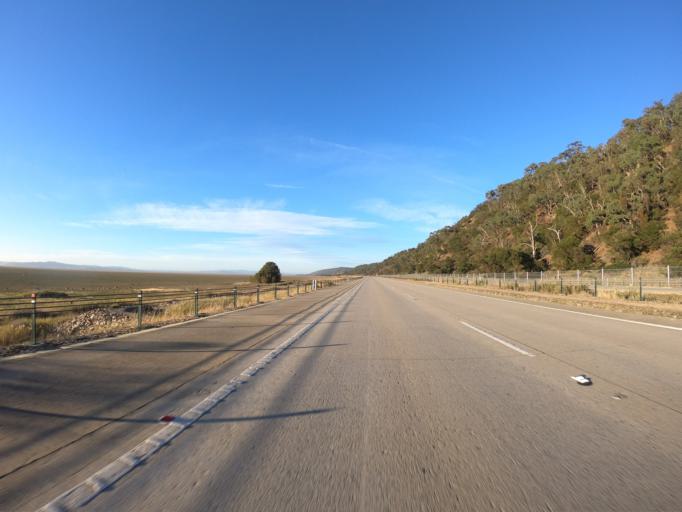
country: AU
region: New South Wales
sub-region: Yass Valley
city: Gundaroo
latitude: -35.0787
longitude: 149.3747
